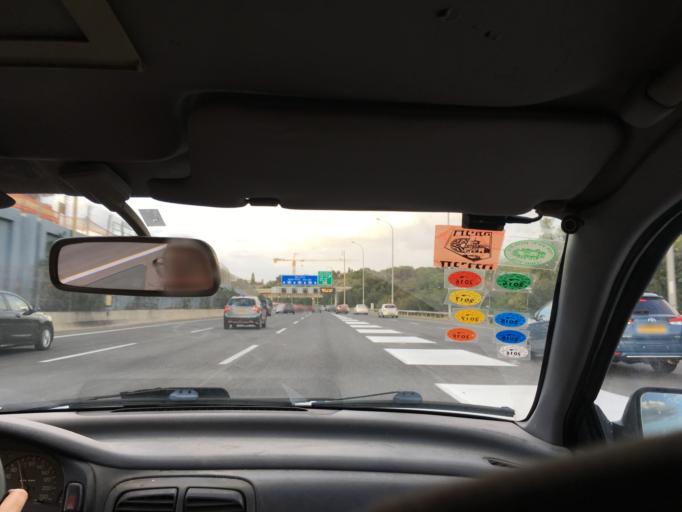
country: IL
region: Tel Aviv
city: Ramat Gan
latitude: 32.1099
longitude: 34.8091
